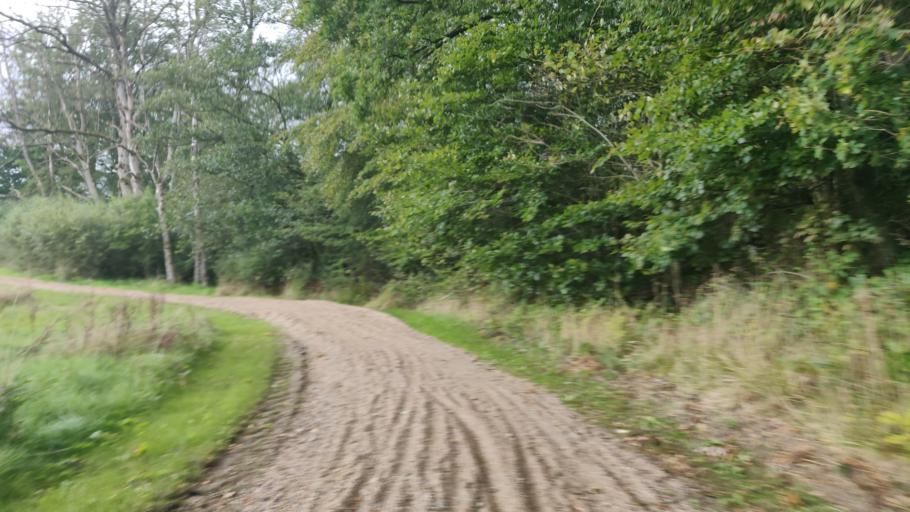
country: DK
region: South Denmark
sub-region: Kolding Kommune
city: Lunderskov
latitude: 55.5393
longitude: 9.3559
